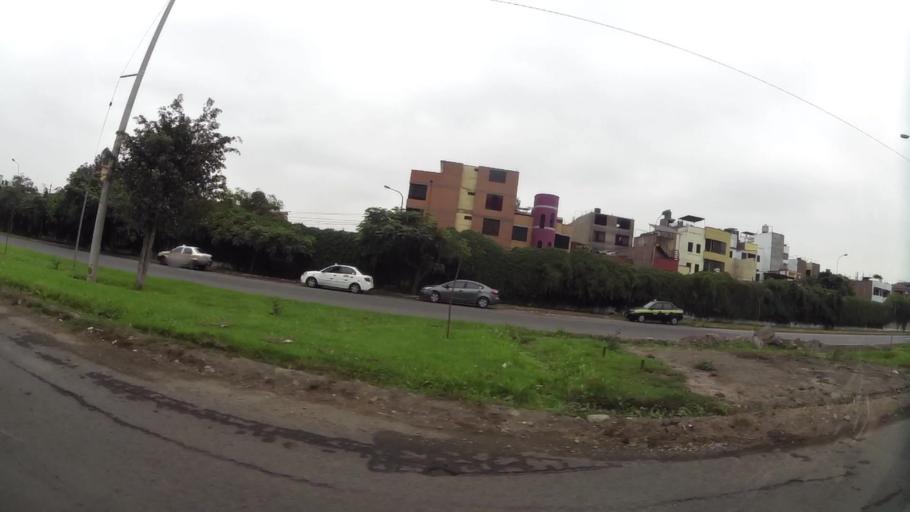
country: PE
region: Lima
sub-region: Lima
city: Vitarte
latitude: -12.0537
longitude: -76.9379
